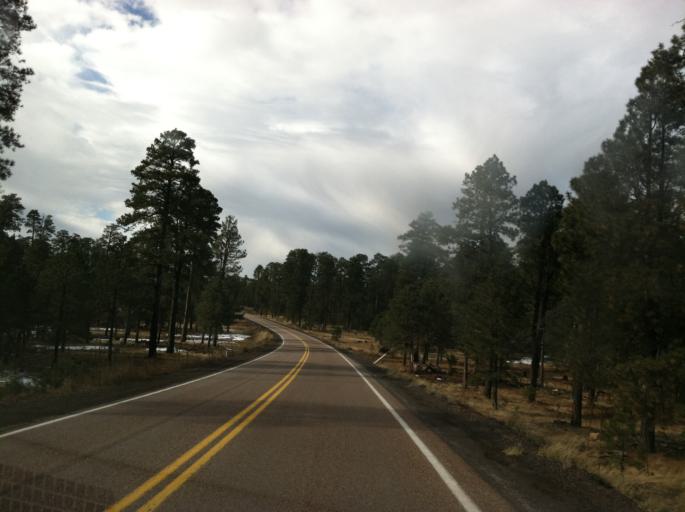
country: US
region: Arizona
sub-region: Navajo County
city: Heber-Overgaard
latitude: 34.3244
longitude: -110.8387
